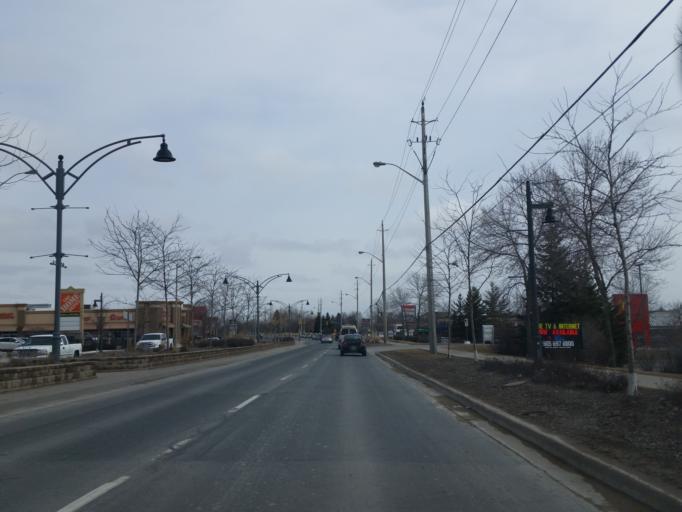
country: CA
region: Ontario
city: Oshawa
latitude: 43.9094
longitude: -78.7105
